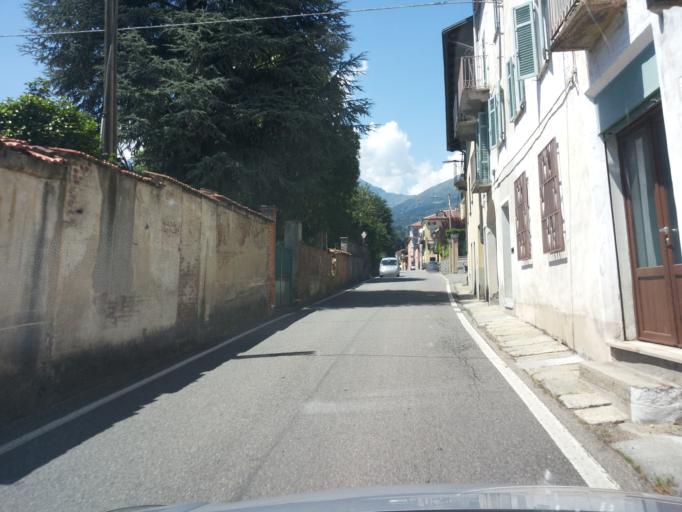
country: IT
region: Piedmont
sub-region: Provincia di Biella
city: Pralungo
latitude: 45.5839
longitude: 8.0361
